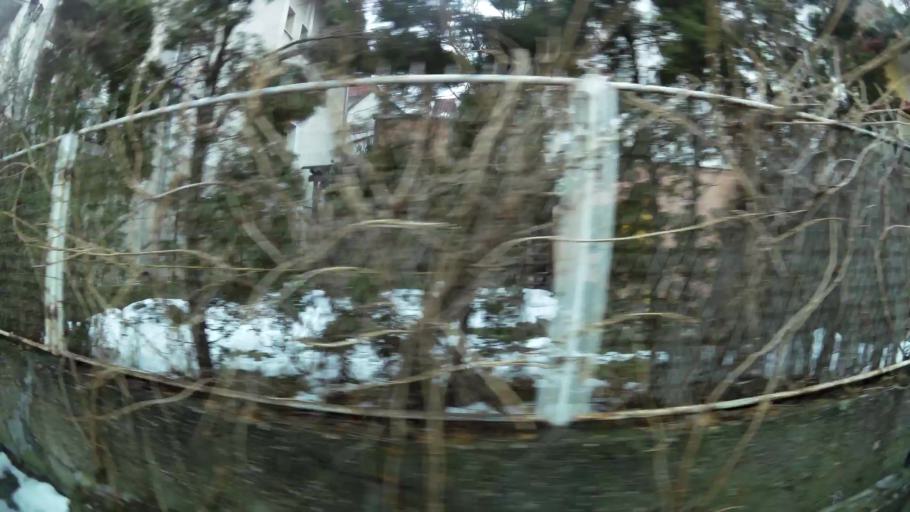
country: RS
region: Central Serbia
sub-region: Belgrade
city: Vozdovac
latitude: 44.7735
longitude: 20.4805
